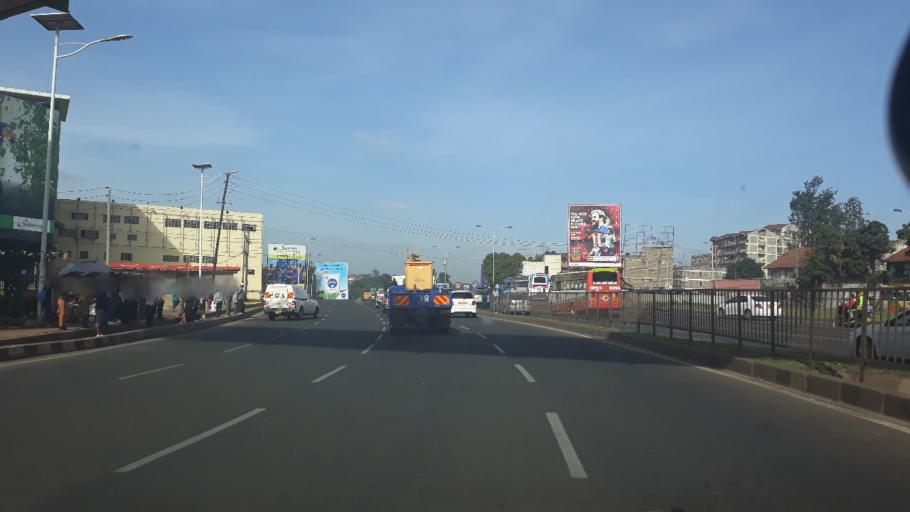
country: KE
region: Nairobi Area
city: Pumwani
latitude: -1.2665
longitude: 36.8343
